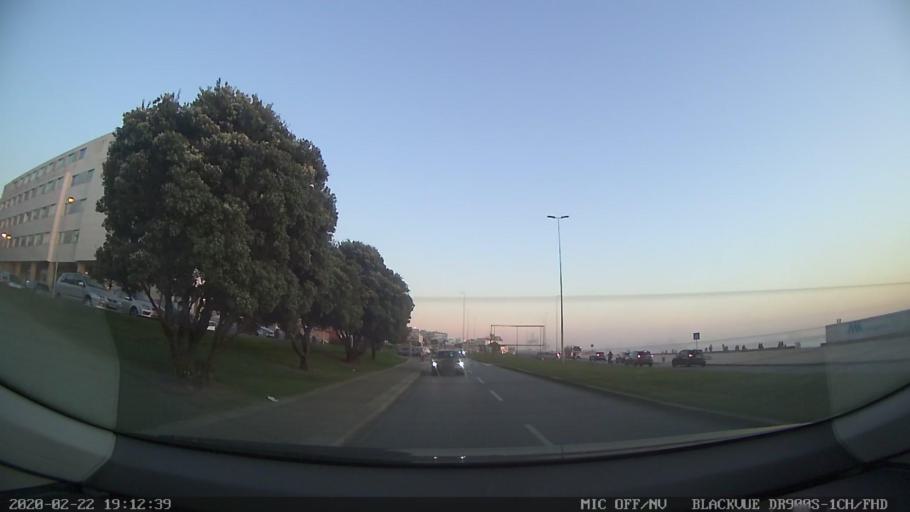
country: PT
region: Porto
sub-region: Matosinhos
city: Leca da Palmeira
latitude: 41.1930
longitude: -8.7066
